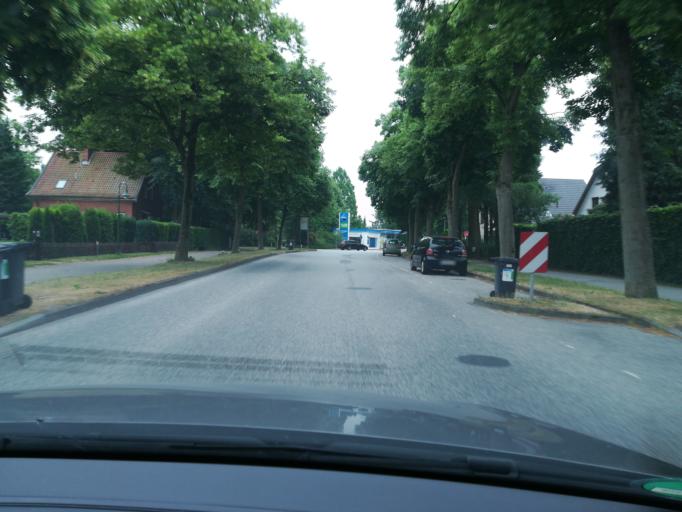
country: DE
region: Schleswig-Holstein
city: Grosshansdorf
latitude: 53.6457
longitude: 10.2767
